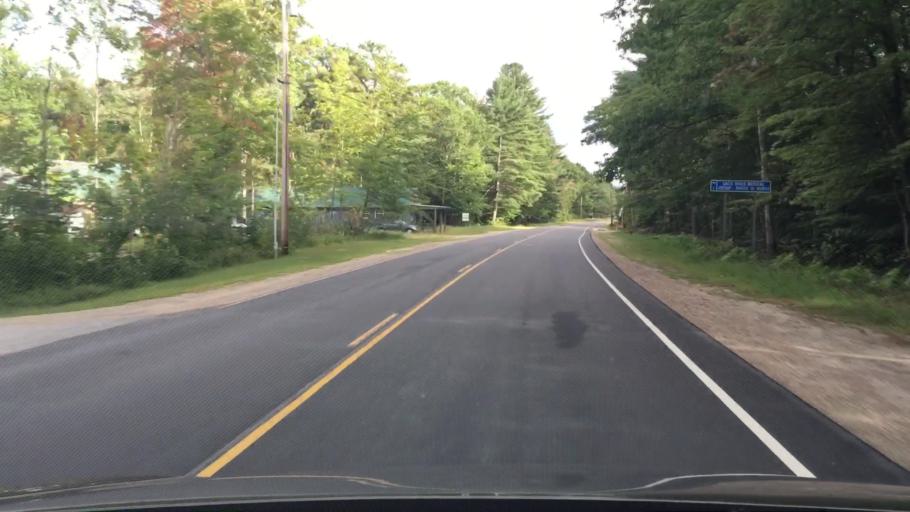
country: US
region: New Hampshire
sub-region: Carroll County
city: Conway
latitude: 43.9825
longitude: -71.1381
